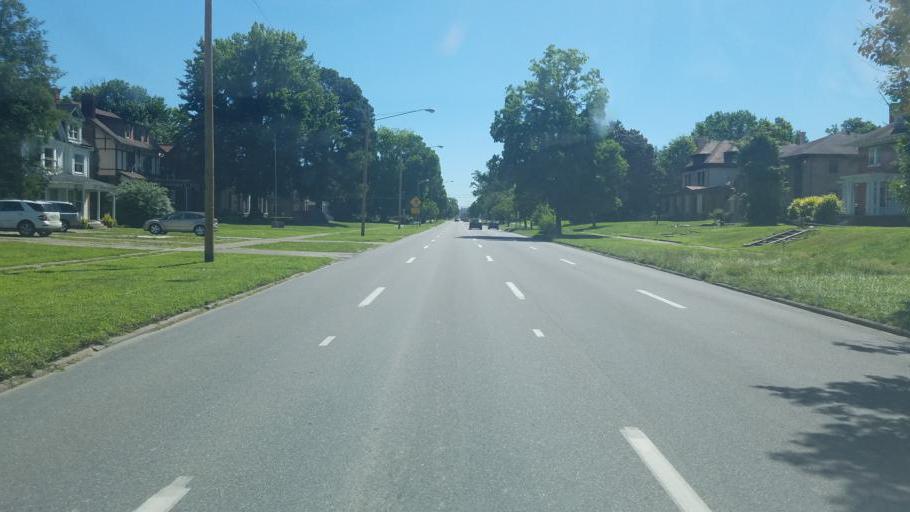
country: US
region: West Virginia
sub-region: Cabell County
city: Huntington
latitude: 38.4209
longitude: -82.4348
